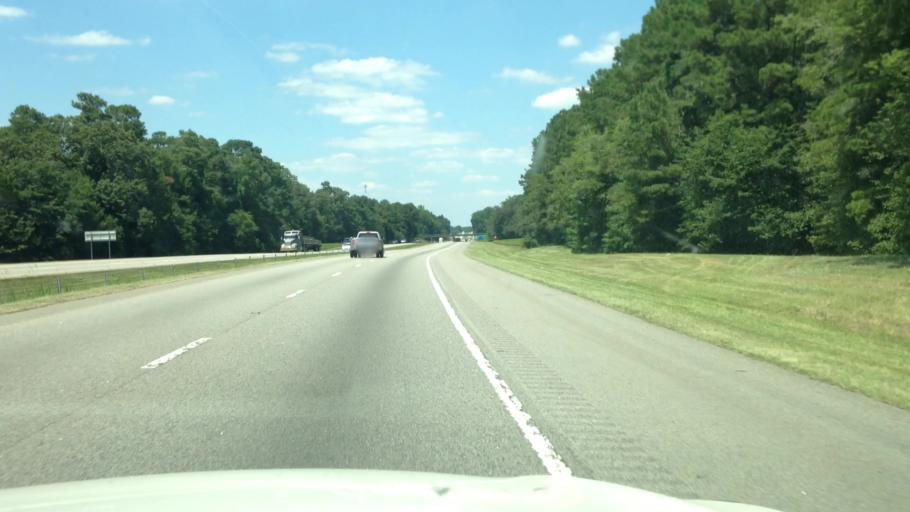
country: US
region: North Carolina
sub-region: Robeson County
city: Saint Pauls
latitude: 34.7938
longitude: -78.9936
